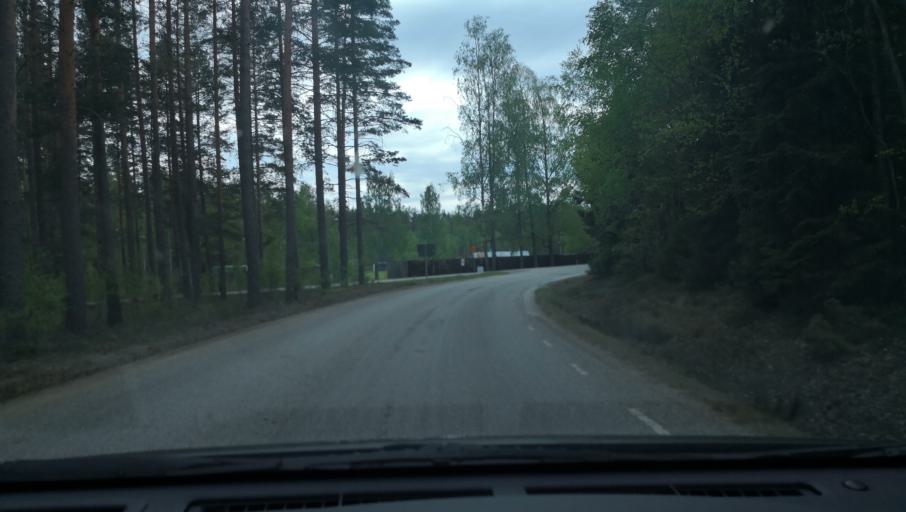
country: SE
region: Vaestmanland
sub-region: Skinnskattebergs Kommun
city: Skinnskatteberg
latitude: 59.8110
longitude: 15.5582
